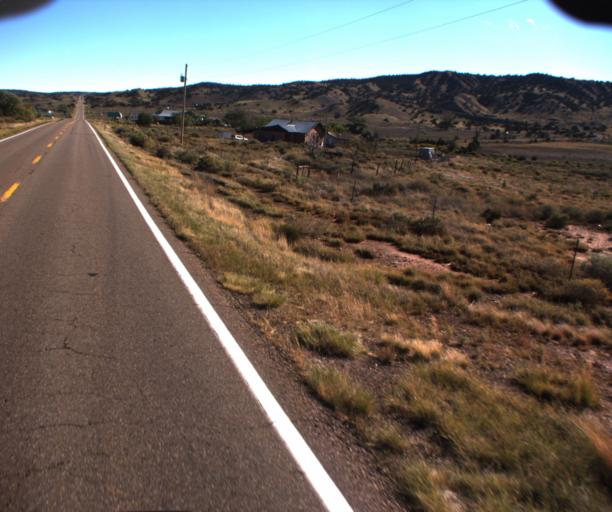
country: US
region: Arizona
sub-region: Apache County
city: Saint Johns
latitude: 34.4735
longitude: -109.6061
